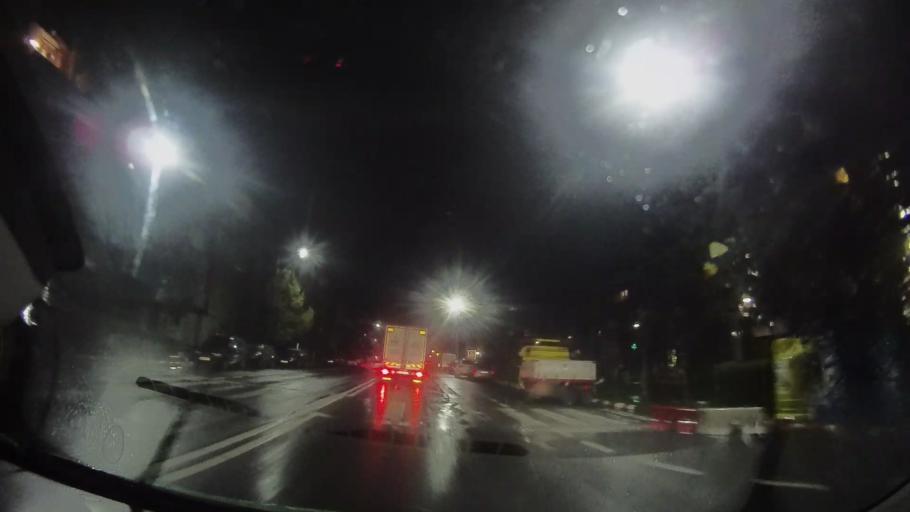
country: RO
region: Mures
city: Reghin-Sat
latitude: 46.7839
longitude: 24.7105
